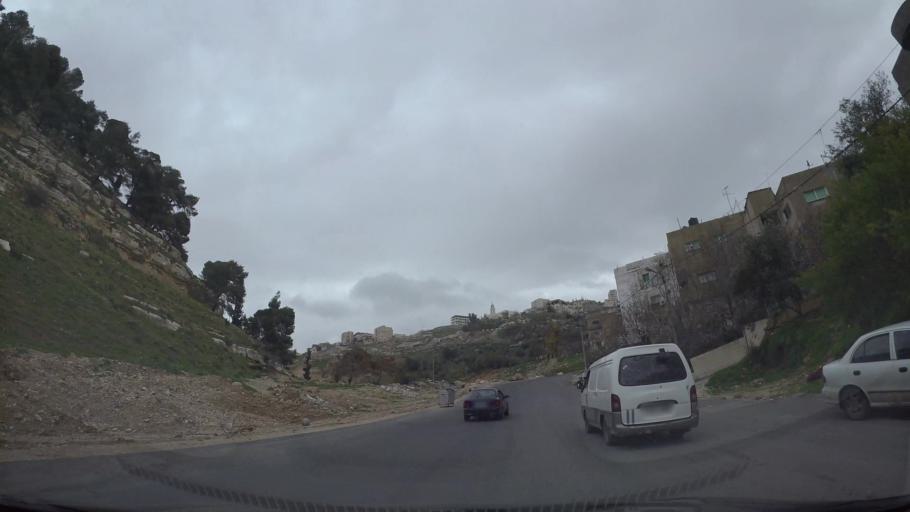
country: JO
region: Amman
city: Wadi as Sir
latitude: 31.9566
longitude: 35.8217
